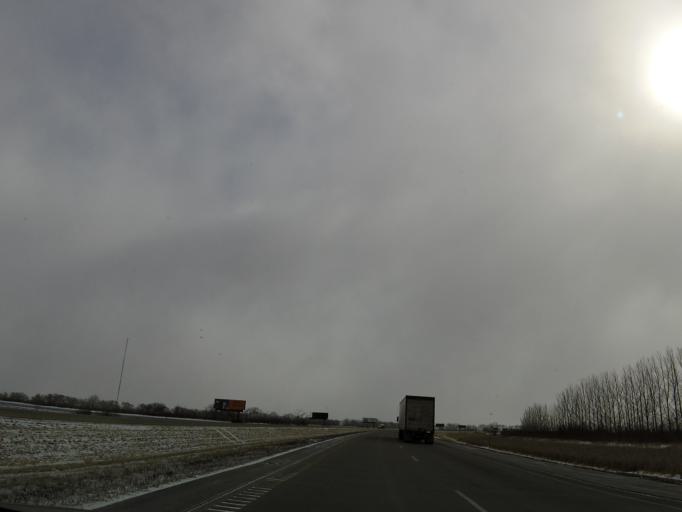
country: US
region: North Dakota
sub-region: Grand Forks County
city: Grand Forks
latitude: 47.8421
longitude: -97.0800
